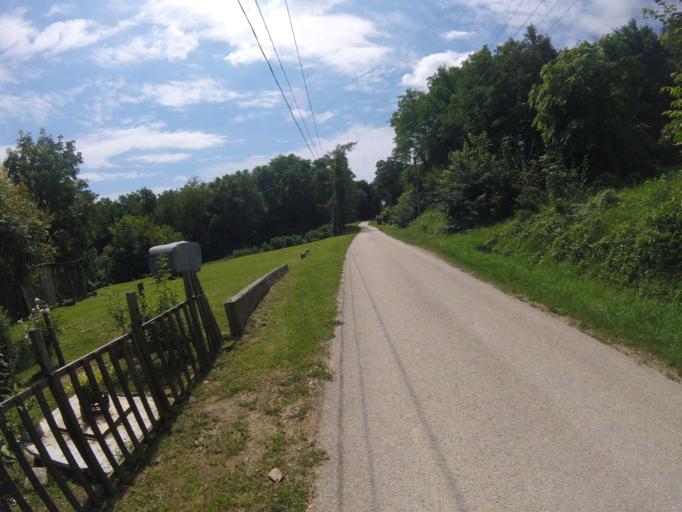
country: HU
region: Zala
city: Nagykanizsa
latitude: 46.5512
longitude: 17.0379
